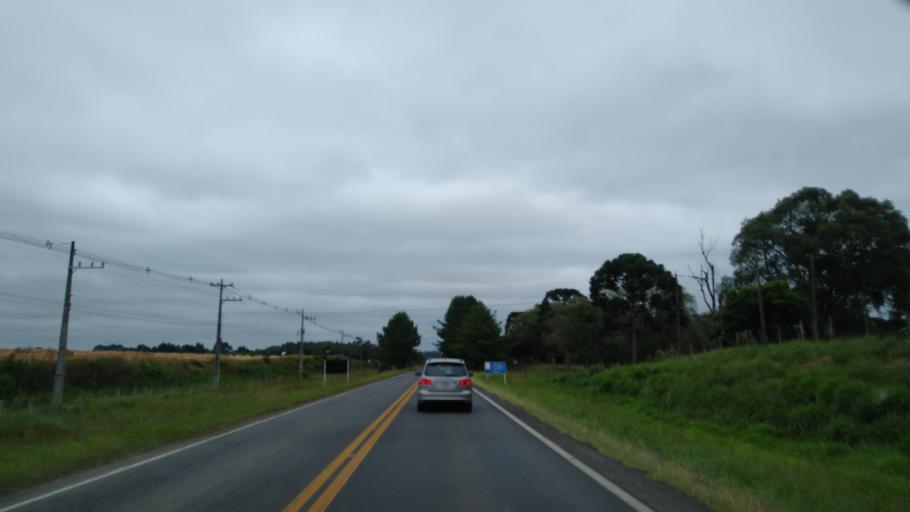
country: BR
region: Santa Catarina
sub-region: Canoinhas
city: Canoinhas
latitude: -26.2329
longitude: -50.4693
